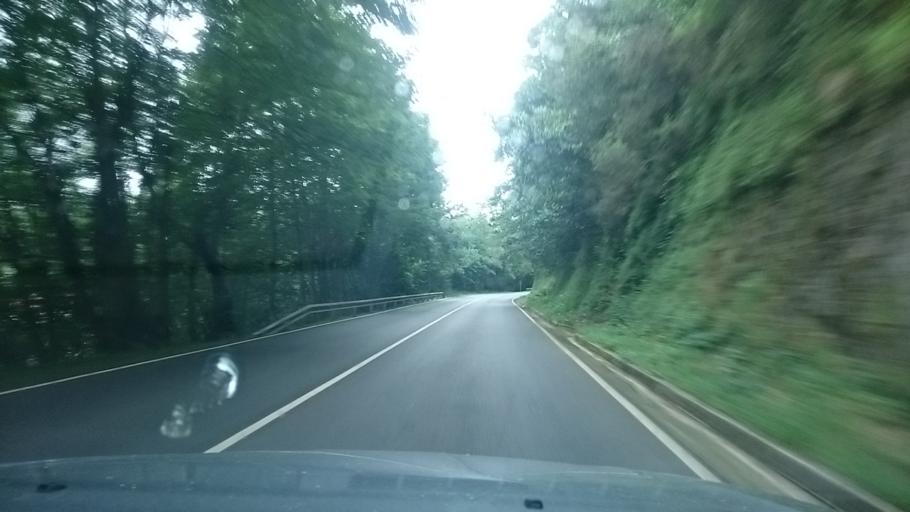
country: ES
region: Asturias
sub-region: Province of Asturias
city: Carrena
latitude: 43.4076
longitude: -4.8901
